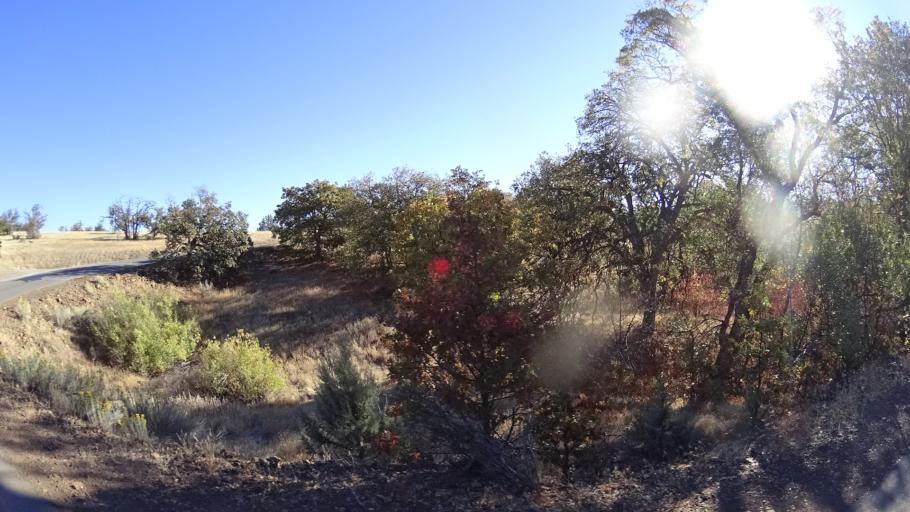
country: US
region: California
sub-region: Siskiyou County
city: Montague
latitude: 41.9499
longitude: -122.4385
